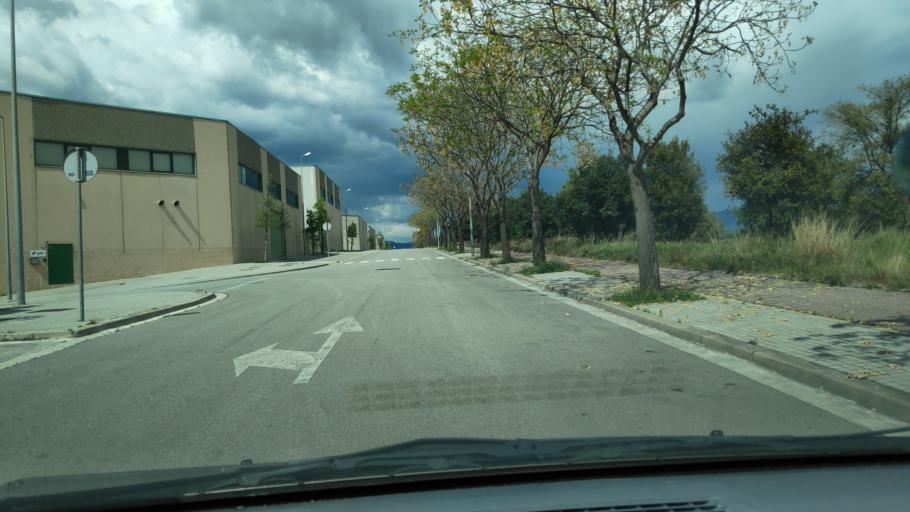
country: ES
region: Catalonia
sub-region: Provincia de Barcelona
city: Polinya
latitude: 41.5397
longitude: 2.1390
